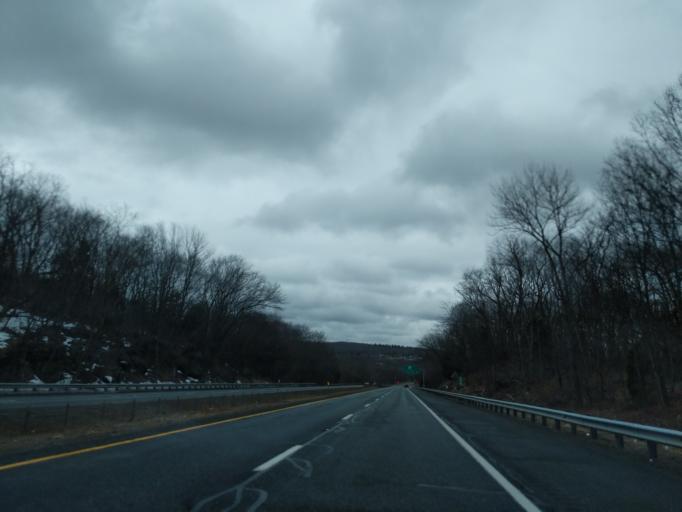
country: US
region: Rhode Island
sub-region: Providence County
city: North Smithfield
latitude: 41.9742
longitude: -71.5257
